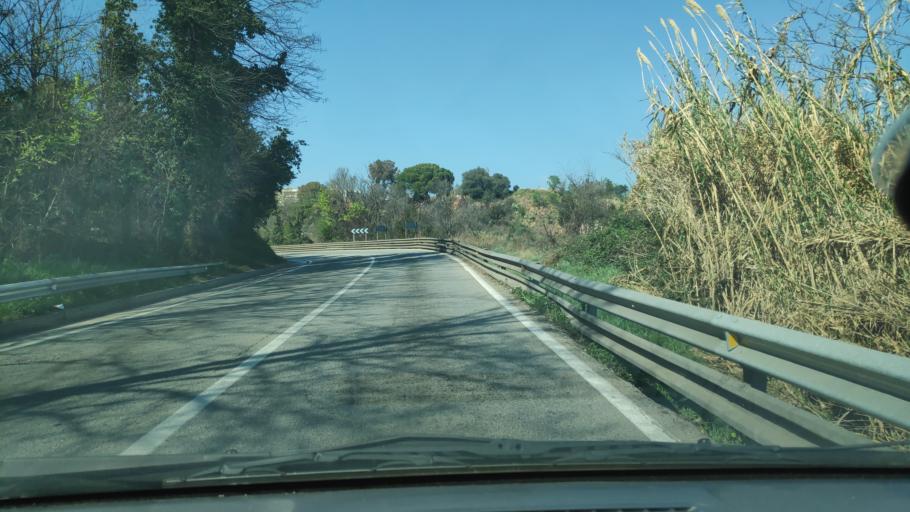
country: ES
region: Catalonia
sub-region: Provincia de Barcelona
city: Barbera del Valles
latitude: 41.5325
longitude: 2.1229
